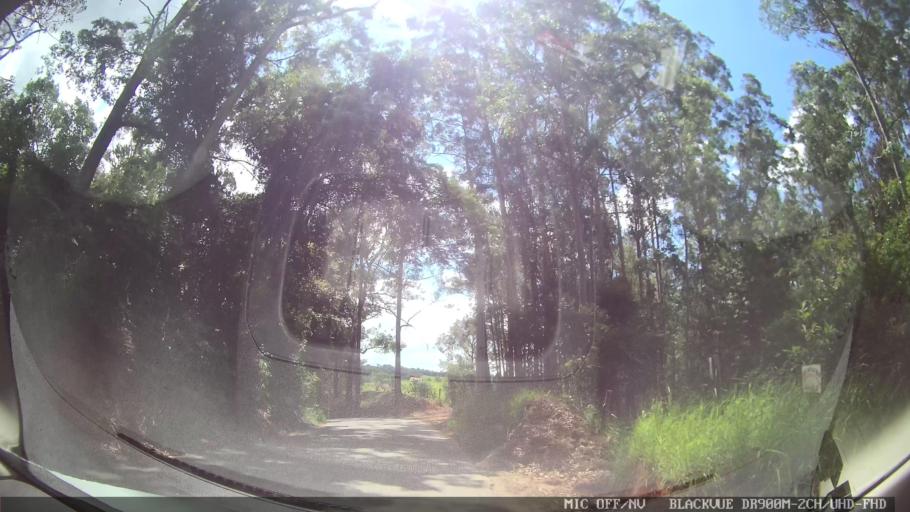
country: BR
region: Minas Gerais
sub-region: Extrema
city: Extrema
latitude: -22.8454
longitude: -46.2832
